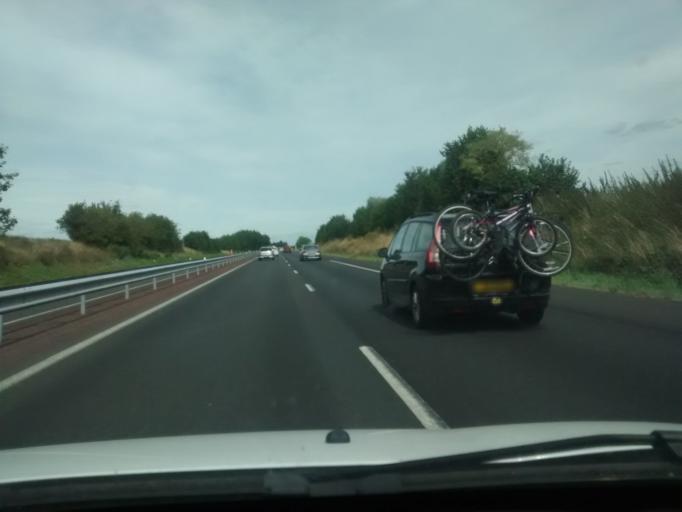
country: FR
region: Lower Normandy
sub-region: Departement de la Manche
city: Saint-James
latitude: 48.5577
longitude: -1.3408
